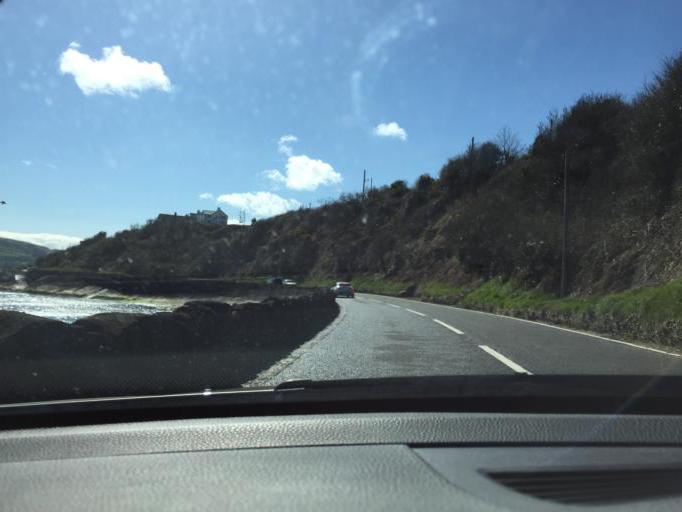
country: GB
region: Northern Ireland
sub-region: Larne District
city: Carnlough
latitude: 55.0011
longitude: -5.9866
